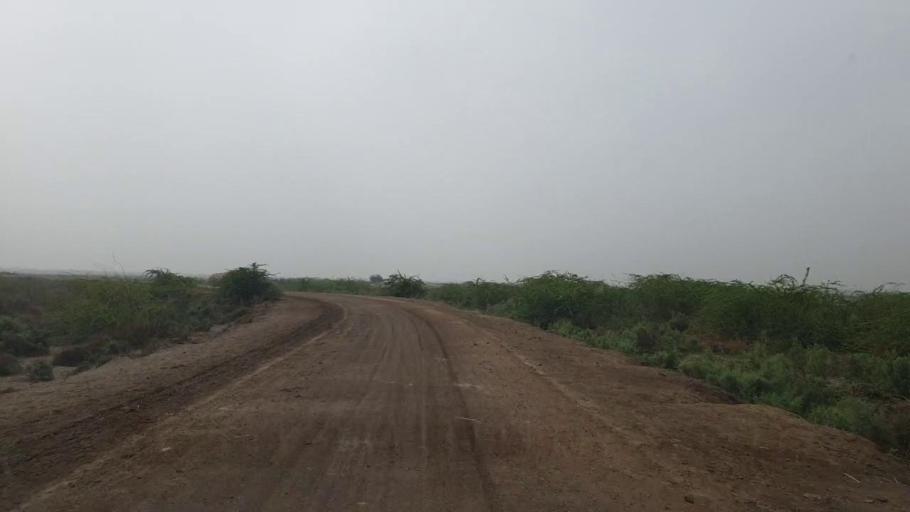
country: PK
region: Sindh
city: Badin
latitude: 24.5826
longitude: 68.6808
